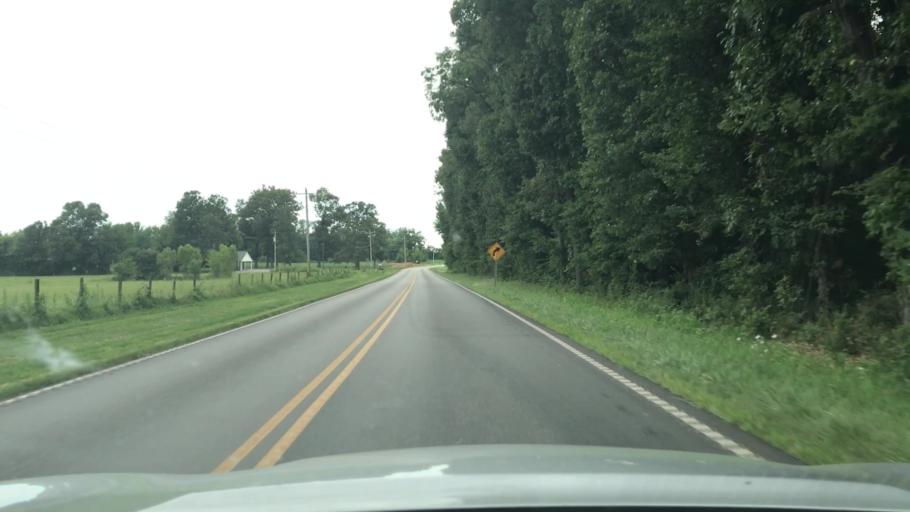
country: US
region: Kentucky
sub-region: Todd County
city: Guthrie
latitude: 36.7271
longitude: -87.1893
